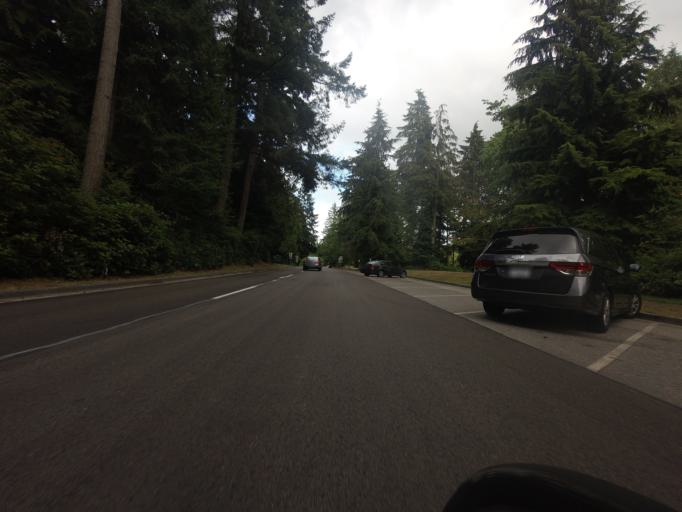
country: CA
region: British Columbia
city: West End
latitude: 49.2965
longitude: -123.1517
